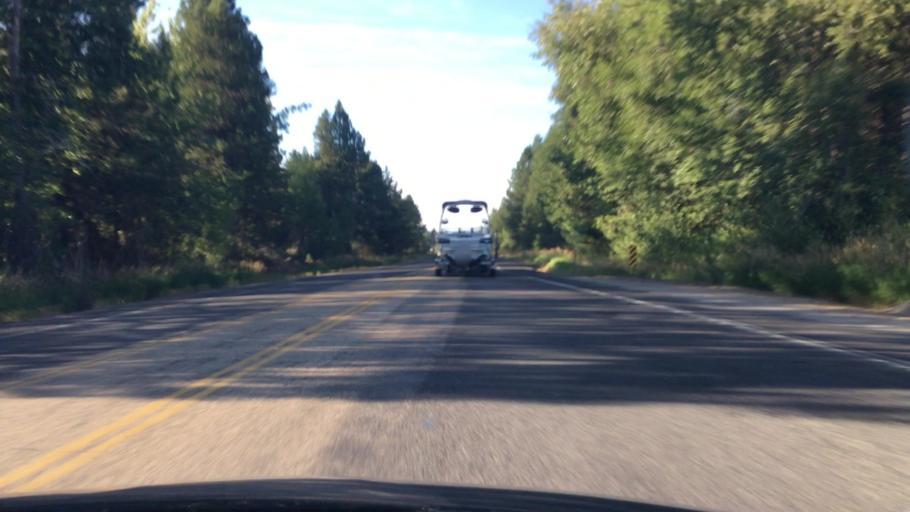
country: US
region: Idaho
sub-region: Valley County
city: Cascade
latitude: 44.6887
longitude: -116.0513
